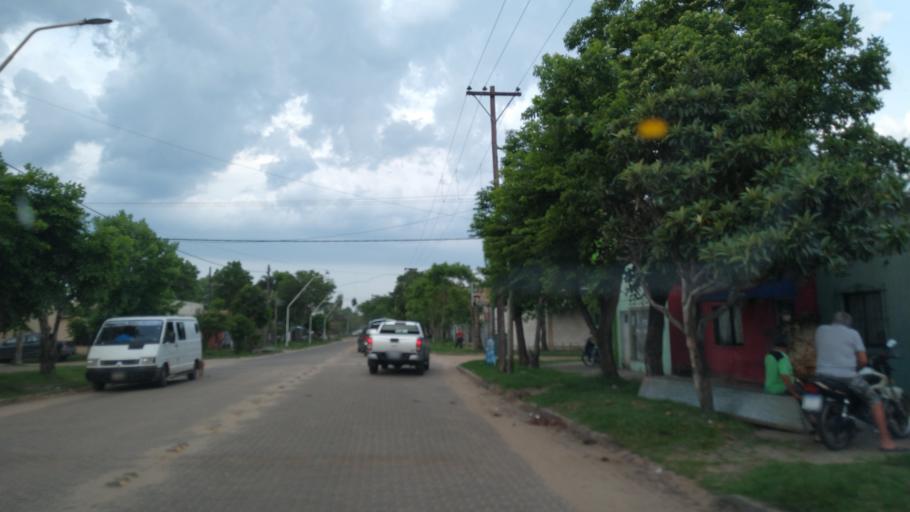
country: AR
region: Corrientes
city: Ituzaingo
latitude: -27.5888
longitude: -56.6978
